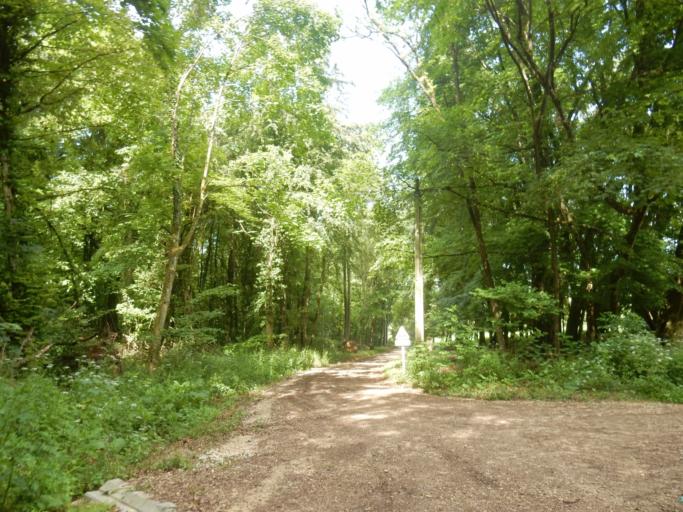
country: FR
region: Lorraine
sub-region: Departement de Meurthe-et-Moselle
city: Pagny-sur-Moselle
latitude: 48.9688
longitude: 5.9857
